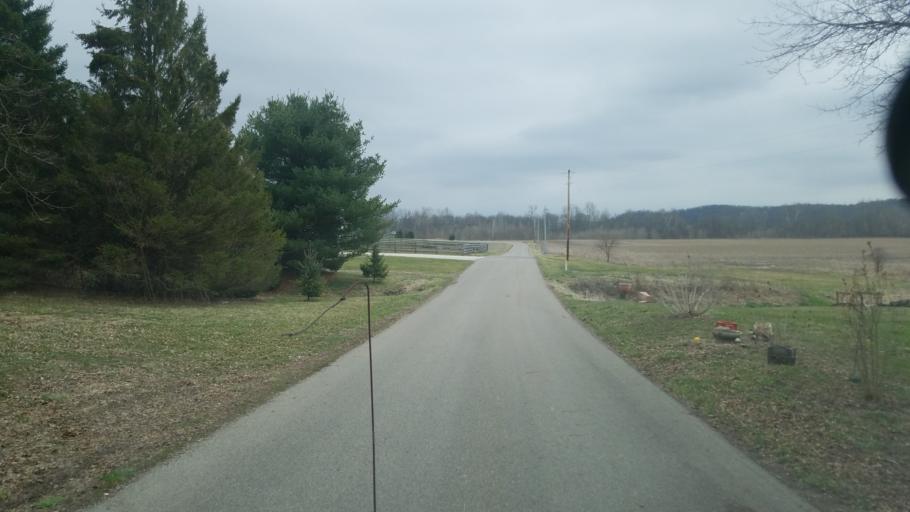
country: US
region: Ohio
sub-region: Licking County
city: Utica
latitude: 40.2017
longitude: -82.4176
